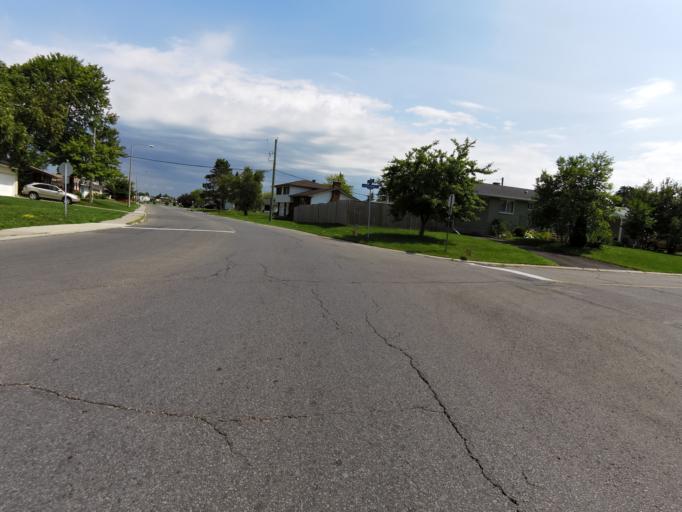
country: CA
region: Quebec
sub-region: Outaouais
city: Gatineau
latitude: 45.4724
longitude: -75.5132
